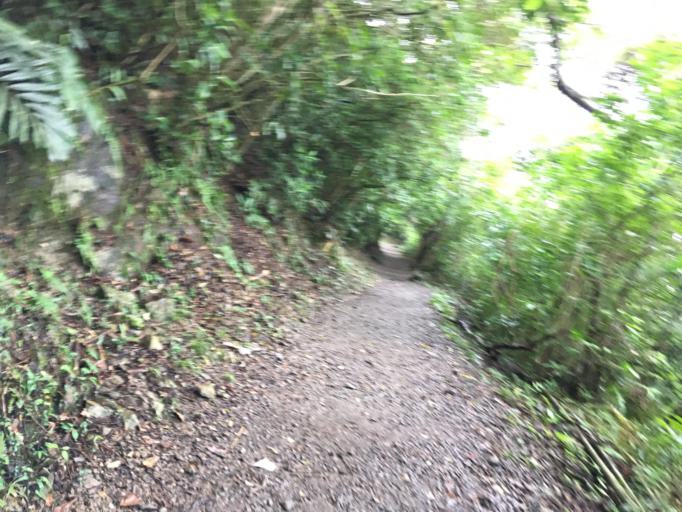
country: TW
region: Taiwan
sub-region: Yilan
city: Yilan
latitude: 24.8389
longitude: 121.7733
